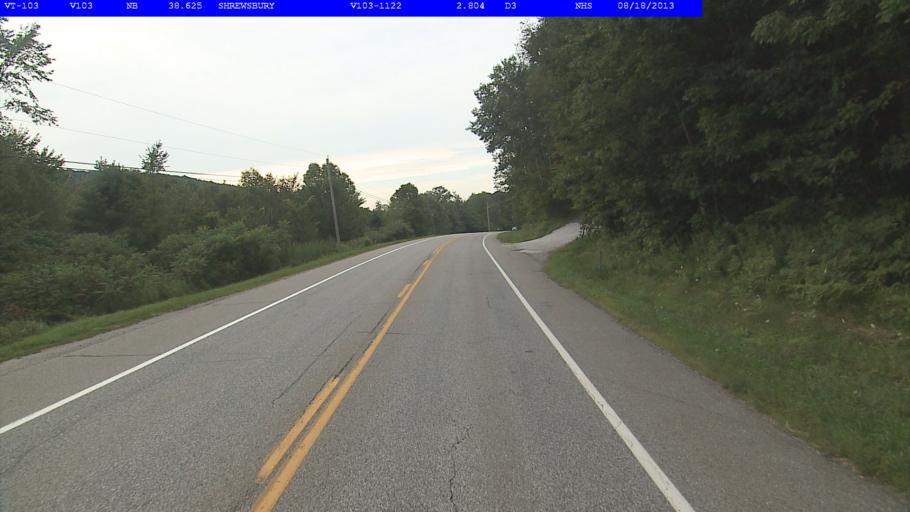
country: US
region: Vermont
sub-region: Rutland County
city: Rutland
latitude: 43.5102
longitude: -72.9104
